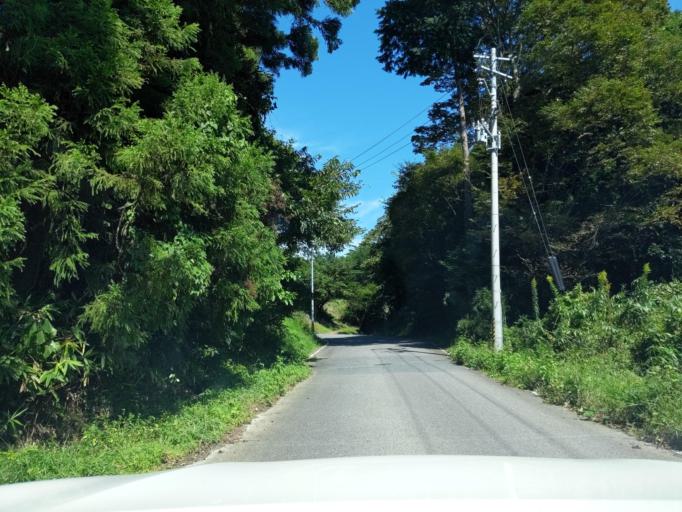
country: JP
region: Fukushima
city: Koriyama
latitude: 37.3766
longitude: 140.2884
